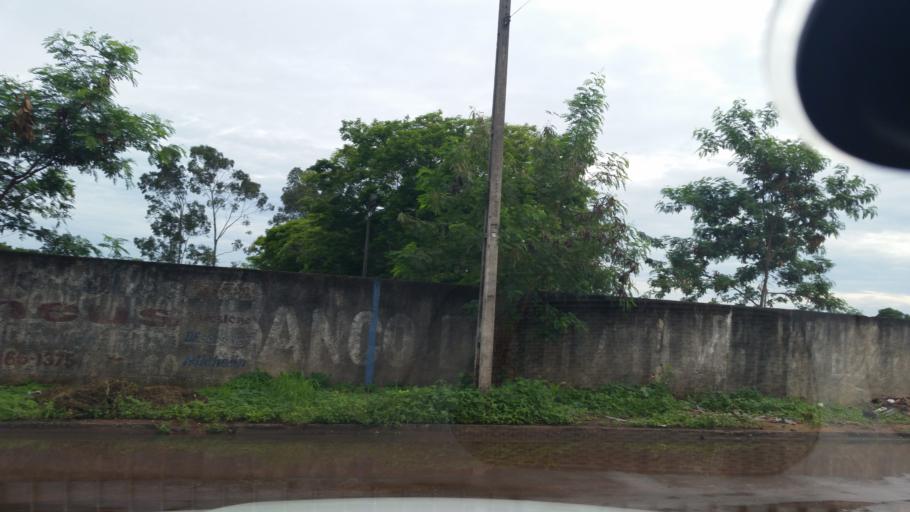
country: BR
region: Goias
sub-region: Uruacu
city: Uruacu
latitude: -14.0173
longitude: -49.1712
